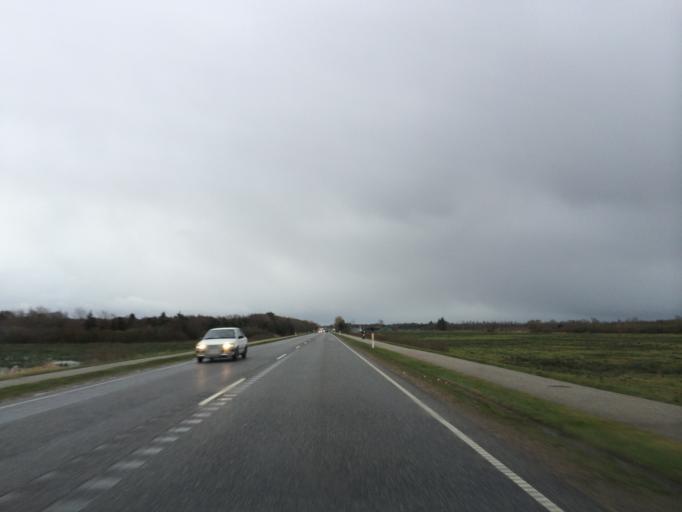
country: DK
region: Central Jutland
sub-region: Ringkobing-Skjern Kommune
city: Tarm
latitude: 55.9252
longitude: 8.5142
